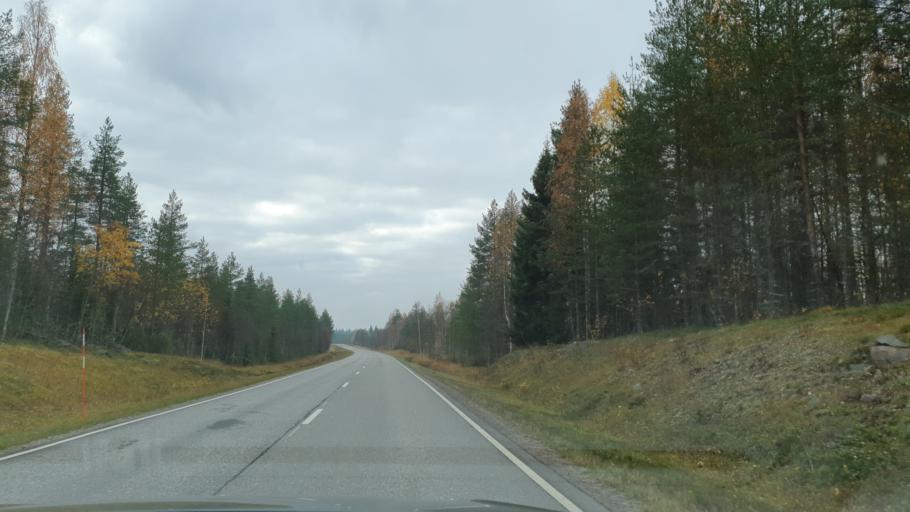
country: FI
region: Lapland
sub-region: Rovaniemi
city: Ranua
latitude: 66.0326
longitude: 26.3306
